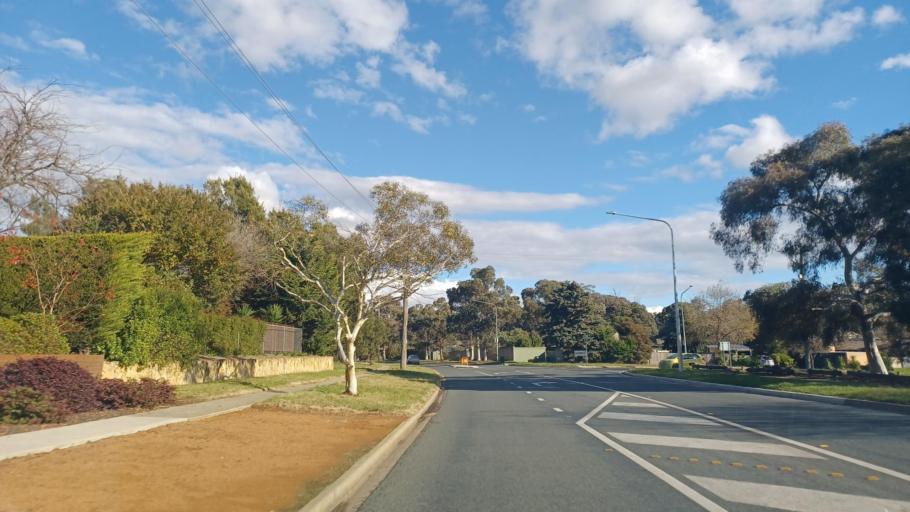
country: AU
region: Australian Capital Territory
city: Belconnen
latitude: -35.1936
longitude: 149.0421
